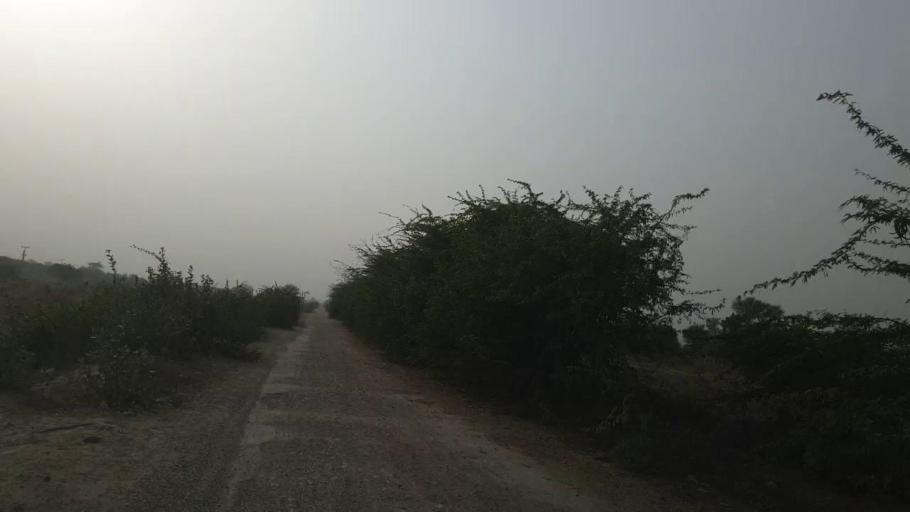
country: PK
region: Sindh
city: Kunri
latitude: 25.0669
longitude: 69.4601
